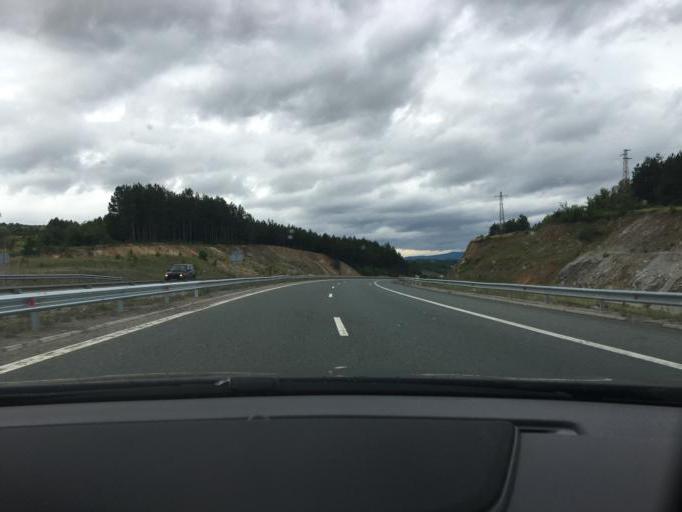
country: BG
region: Pernik
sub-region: Obshtina Pernik
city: Pernik
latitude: 42.5003
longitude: 23.1393
